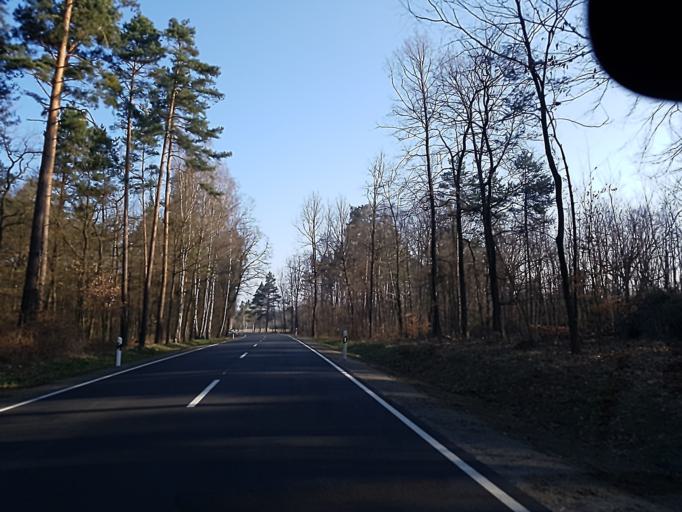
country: DE
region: Brandenburg
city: Bronkow
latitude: 51.6975
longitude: 13.9191
